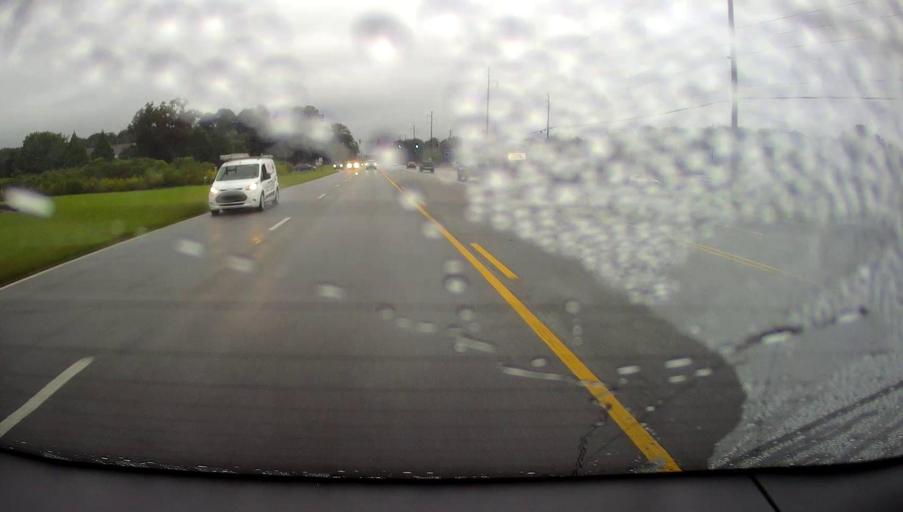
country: US
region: Georgia
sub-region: Houston County
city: Centerville
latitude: 32.6042
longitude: -83.6746
